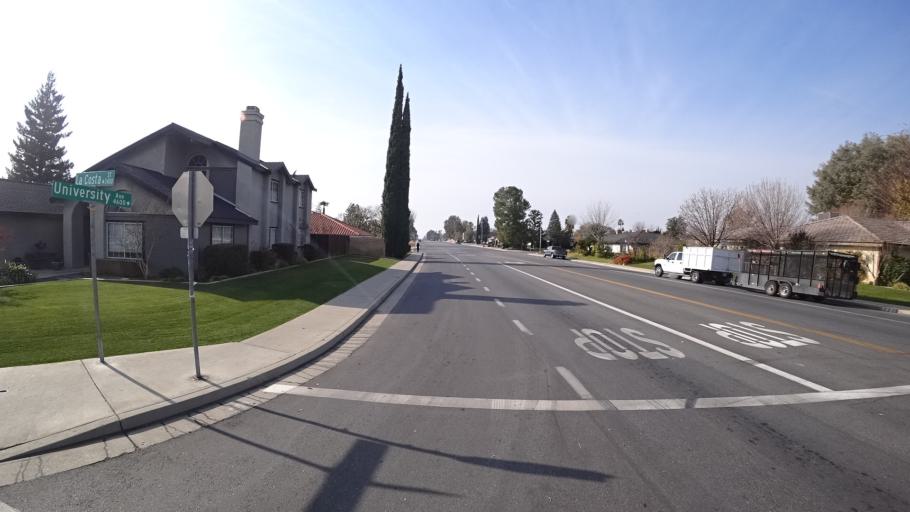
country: US
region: California
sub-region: Kern County
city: Oildale
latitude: 35.4051
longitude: -118.9411
